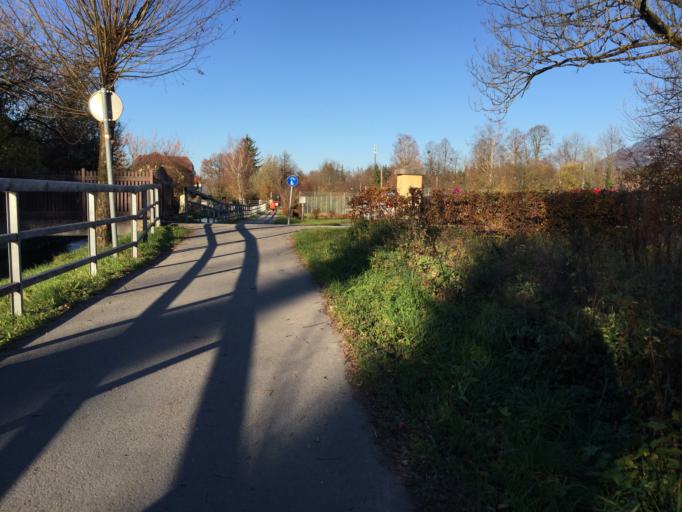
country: AT
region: Salzburg
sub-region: Politischer Bezirk Salzburg-Umgebung
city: Grodig
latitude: 47.7630
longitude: 13.0388
